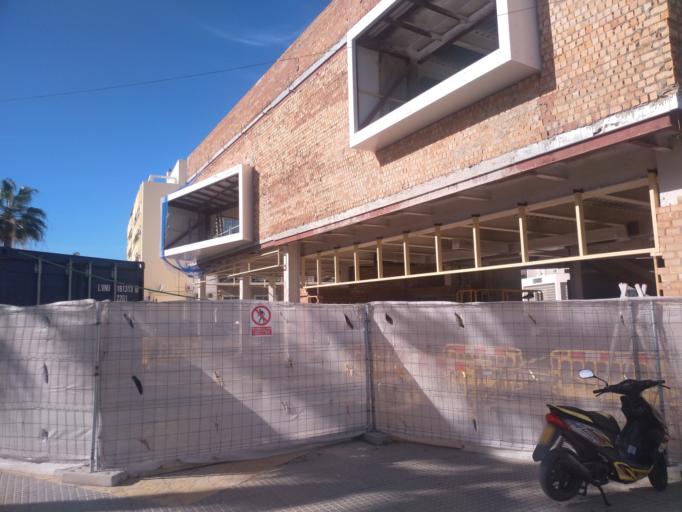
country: ES
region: Andalusia
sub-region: Provincia de Cadiz
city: San Fernando
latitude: 36.4681
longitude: -6.1900
